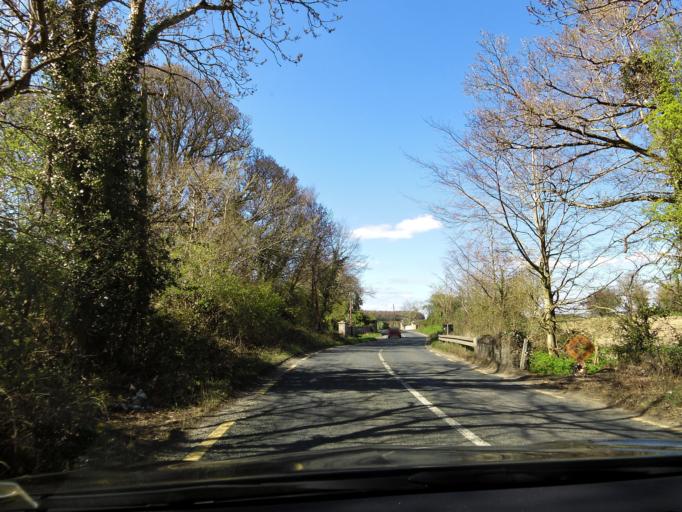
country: IE
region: Leinster
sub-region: Laois
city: Stradbally
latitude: 53.0141
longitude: -7.0861
